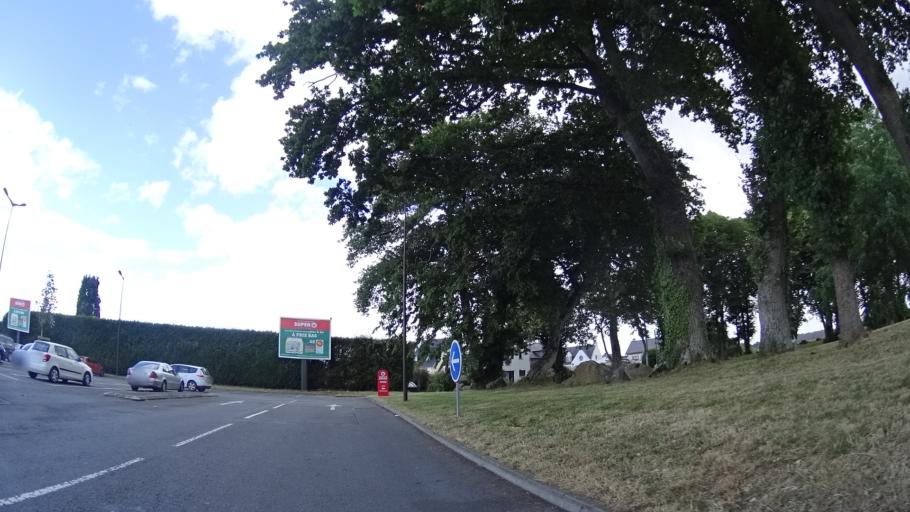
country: FR
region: Brittany
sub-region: Departement d'Ille-et-Vilaine
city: Tinteniac
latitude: 48.3297
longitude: -1.8407
